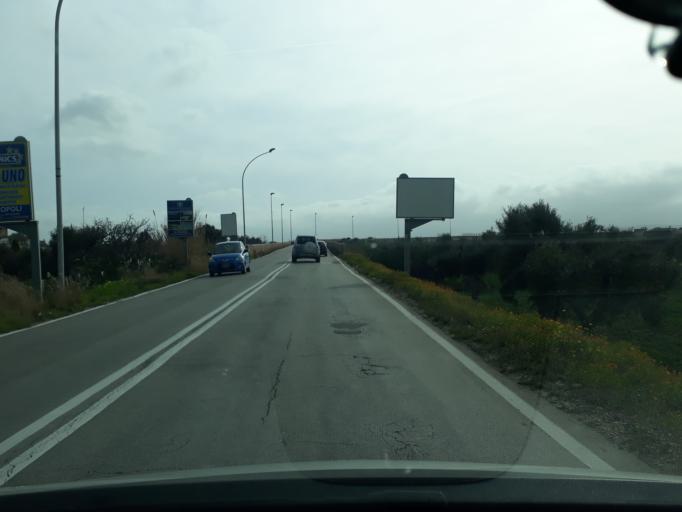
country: IT
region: Apulia
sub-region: Provincia di Bari
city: Monopoli
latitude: 40.9592
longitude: 17.2821
